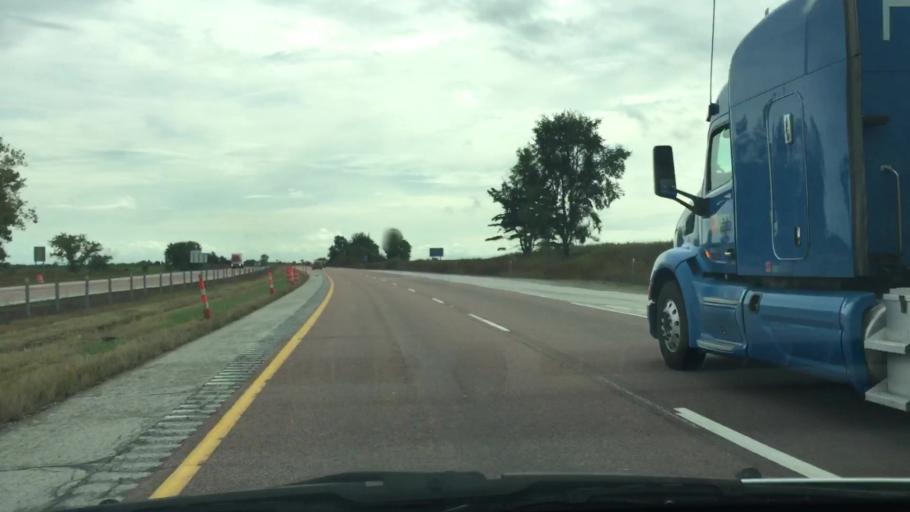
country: US
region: Iowa
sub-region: Warren County
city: Norwalk
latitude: 41.2920
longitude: -93.7802
